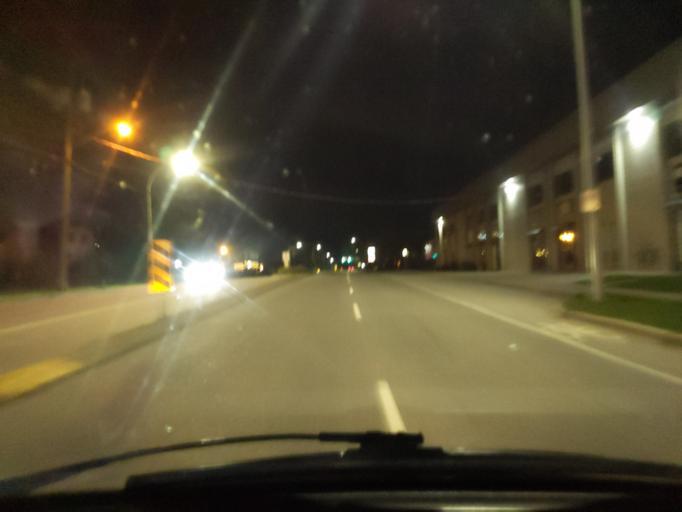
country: CA
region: British Columbia
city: Pitt Meadows
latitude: 49.1761
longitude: -122.6907
